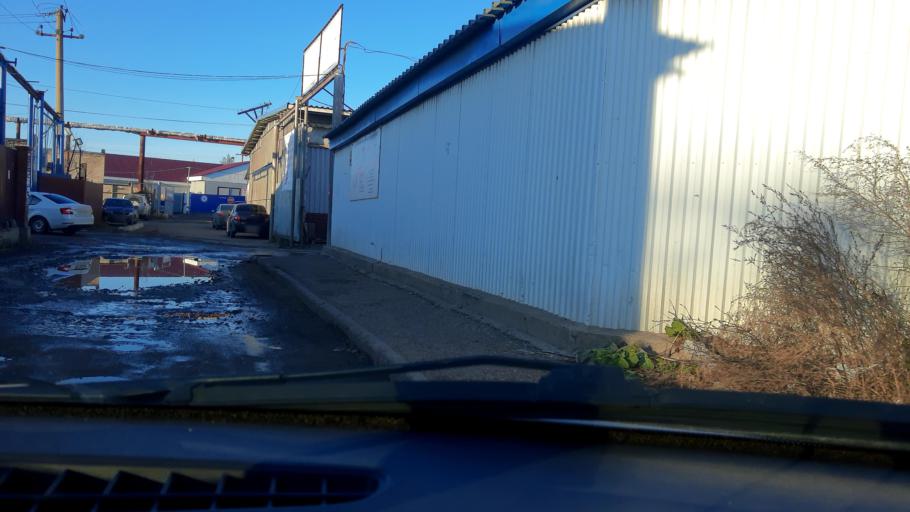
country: RU
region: Bashkortostan
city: Mikhaylovka
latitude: 54.6938
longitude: 55.8432
